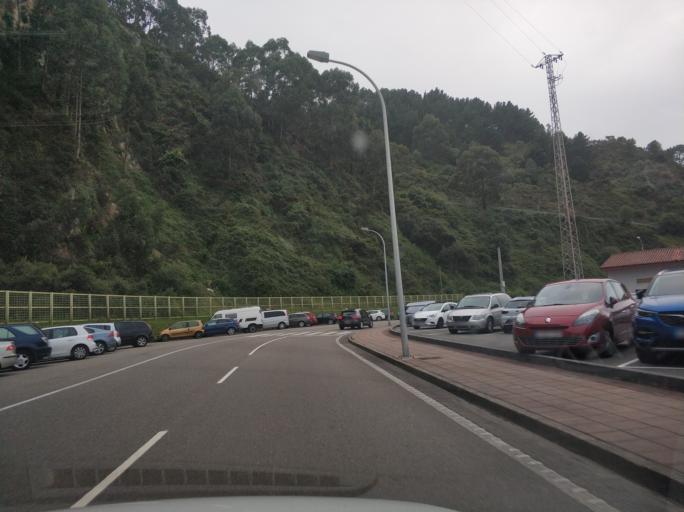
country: ES
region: Asturias
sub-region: Province of Asturias
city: Cudillero
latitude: 43.5655
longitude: -6.1512
